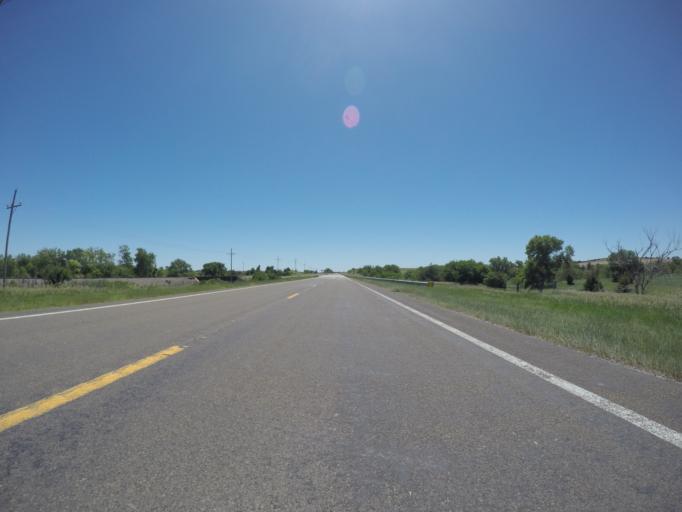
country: US
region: Kansas
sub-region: Phillips County
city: Phillipsburg
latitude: 39.8033
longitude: -99.4742
